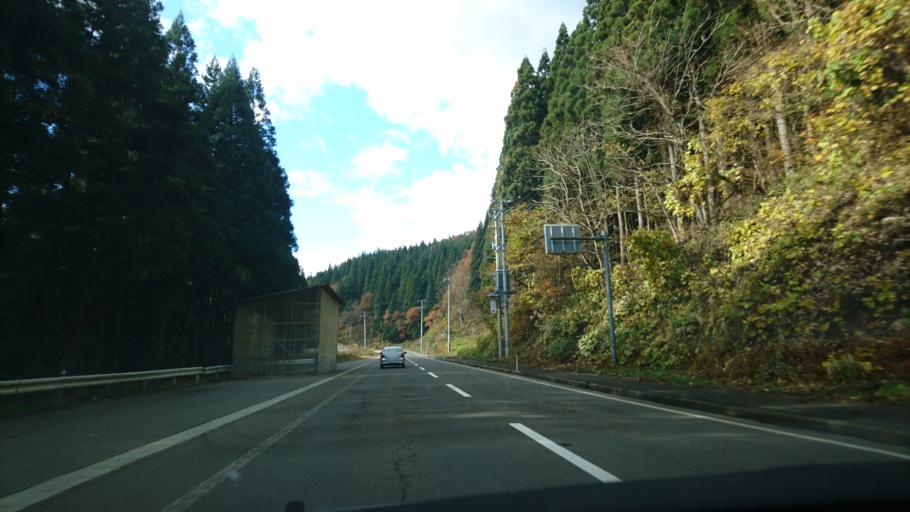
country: JP
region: Akita
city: Yuzawa
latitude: 39.2745
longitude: 140.3611
